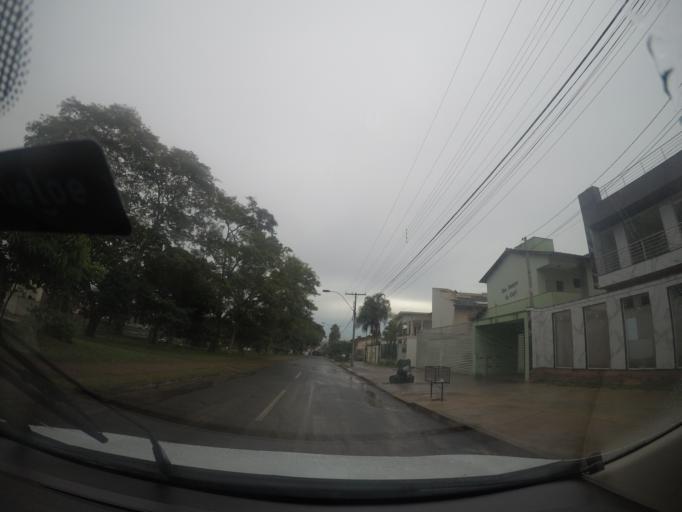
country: BR
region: Goias
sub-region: Goiania
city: Goiania
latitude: -16.6375
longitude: -49.2341
